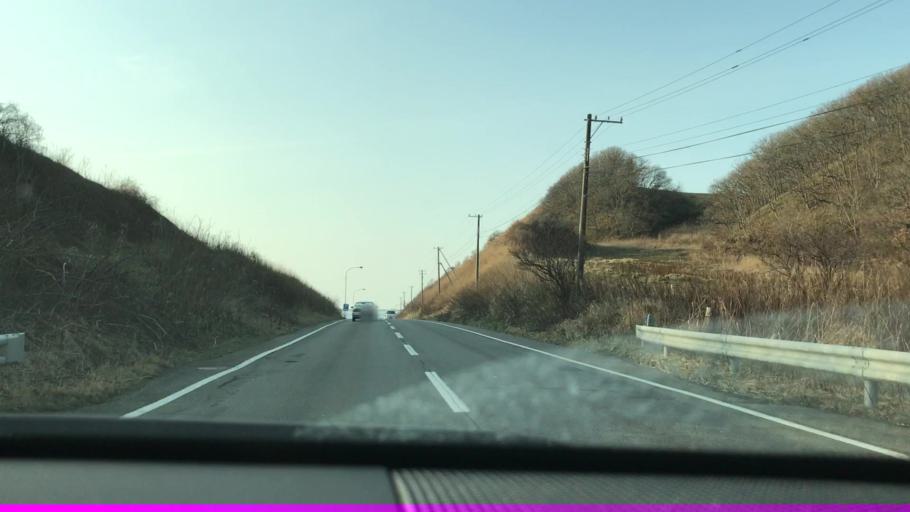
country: JP
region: Hokkaido
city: Shizunai-furukawacho
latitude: 42.2321
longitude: 142.6077
